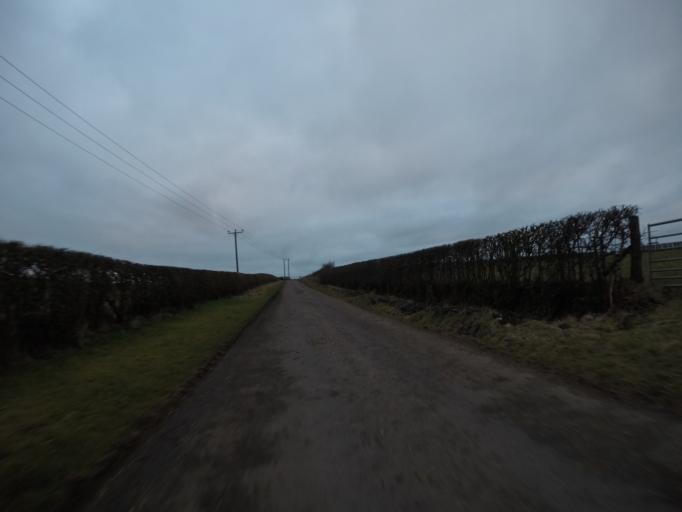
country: GB
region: Scotland
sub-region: North Ayrshire
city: Dalry
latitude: 55.6893
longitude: -4.7420
